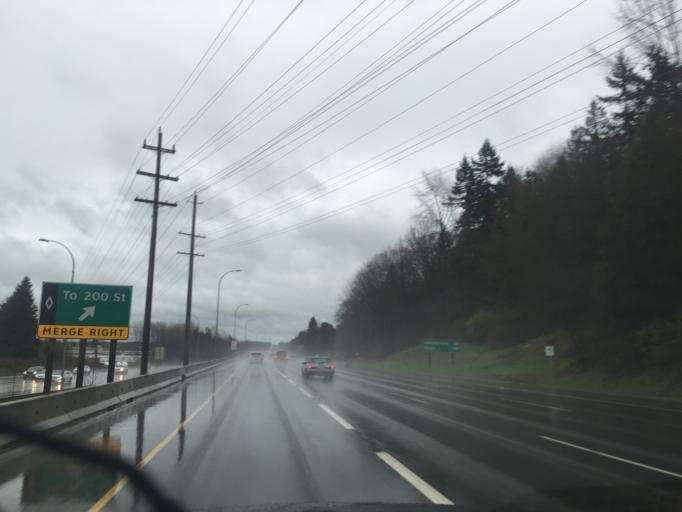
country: CA
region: British Columbia
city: Pitt Meadows
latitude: 49.1753
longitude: -122.7116
